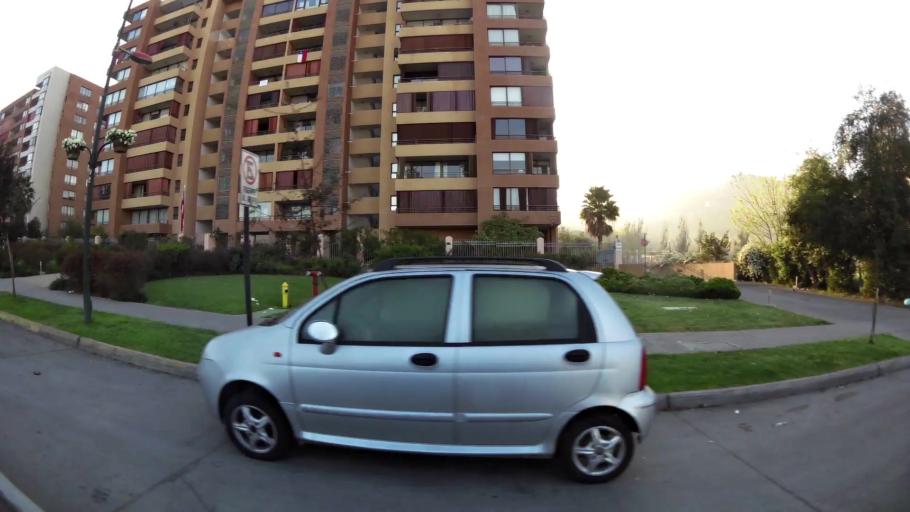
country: CL
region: Santiago Metropolitan
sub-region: Provincia de Santiago
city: Santiago
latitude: -33.3857
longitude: -70.6148
